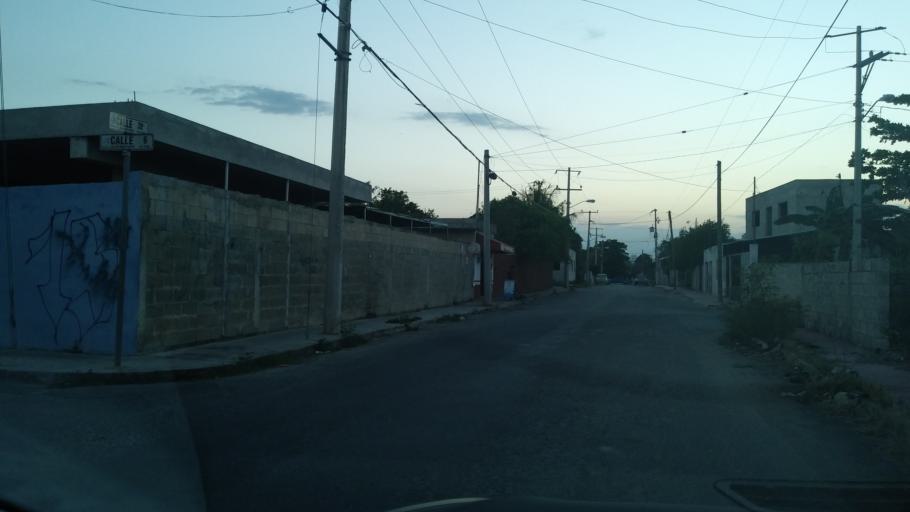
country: MX
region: Yucatan
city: Itzincab Palomeque
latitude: 20.9279
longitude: -89.6706
